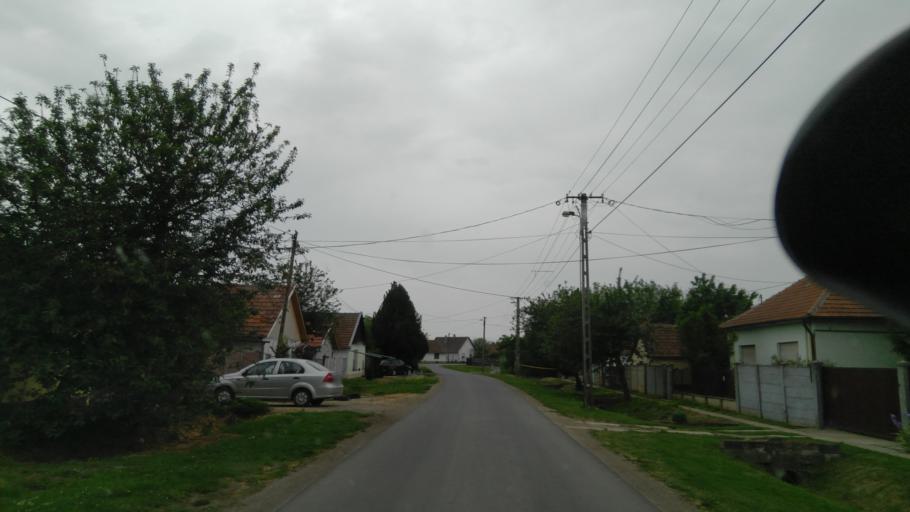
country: HU
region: Bekes
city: Doboz
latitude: 46.7274
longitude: 21.2445
